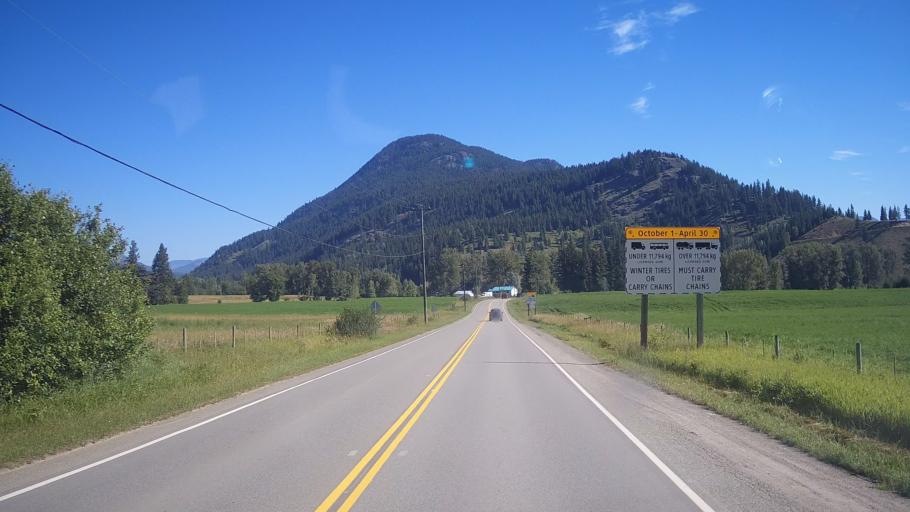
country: CA
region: British Columbia
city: Kamloops
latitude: 51.4274
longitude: -120.2113
